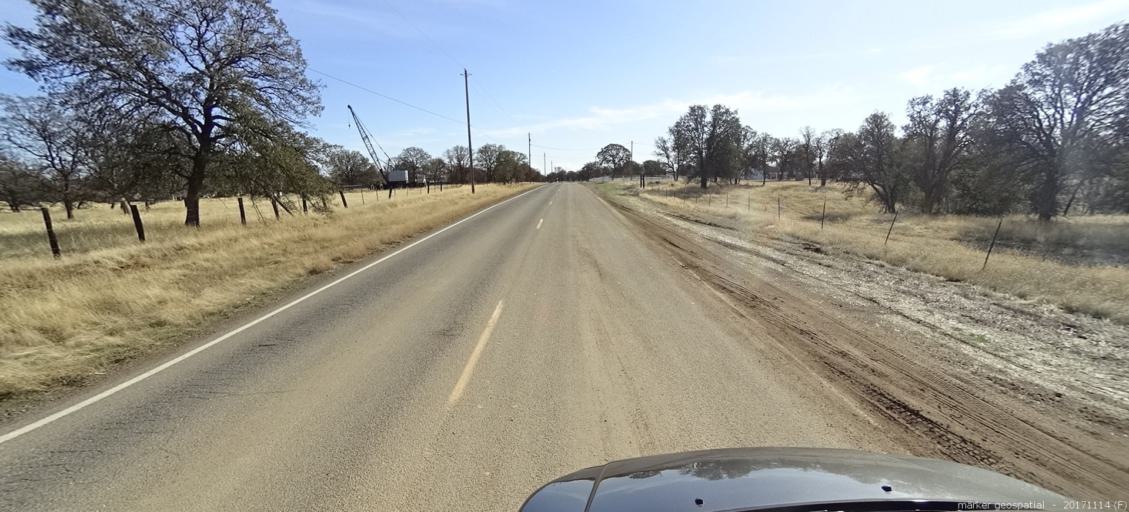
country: US
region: California
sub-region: Shasta County
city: Anderson
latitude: 40.4146
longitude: -122.3483
